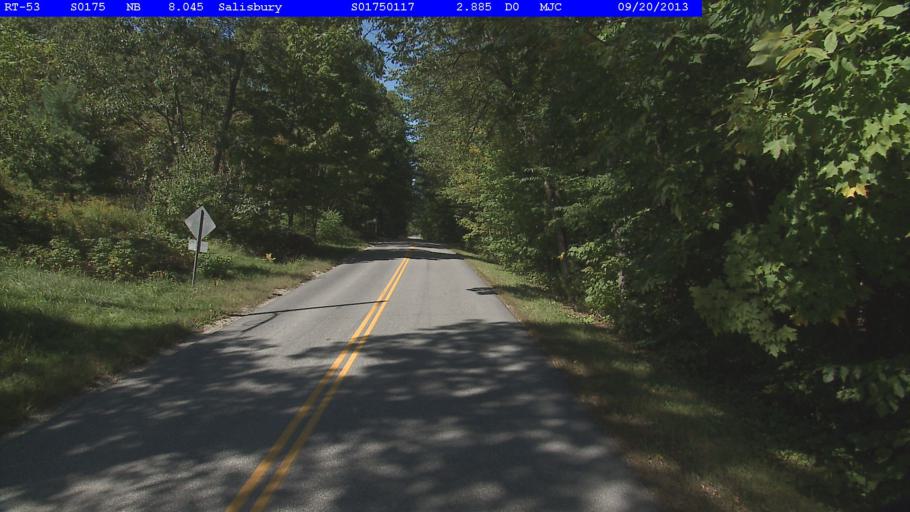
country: US
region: Vermont
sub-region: Rutland County
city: Brandon
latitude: 43.9209
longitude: -73.0881
